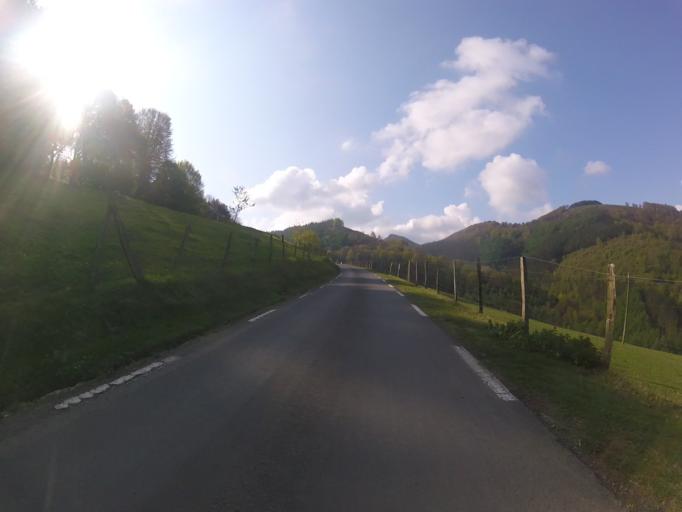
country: ES
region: Basque Country
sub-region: Provincia de Guipuzcoa
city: Azkoitia
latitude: 43.2258
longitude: -2.3189
